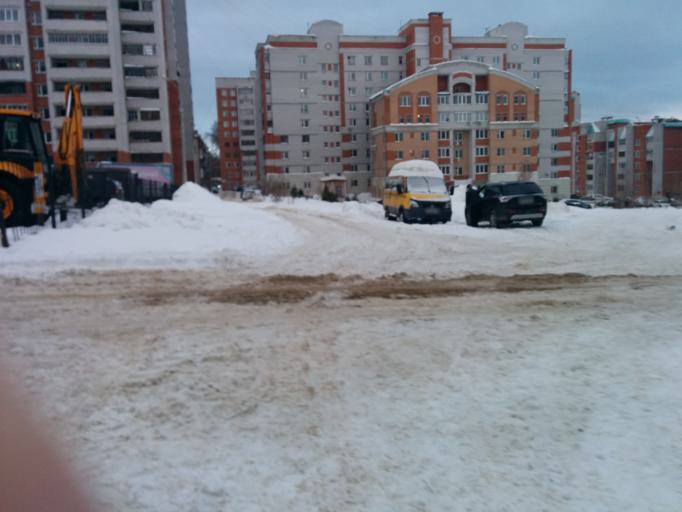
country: RU
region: Chuvashia
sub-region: Cheboksarskiy Rayon
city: Cheboksary
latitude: 56.1293
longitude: 47.2659
